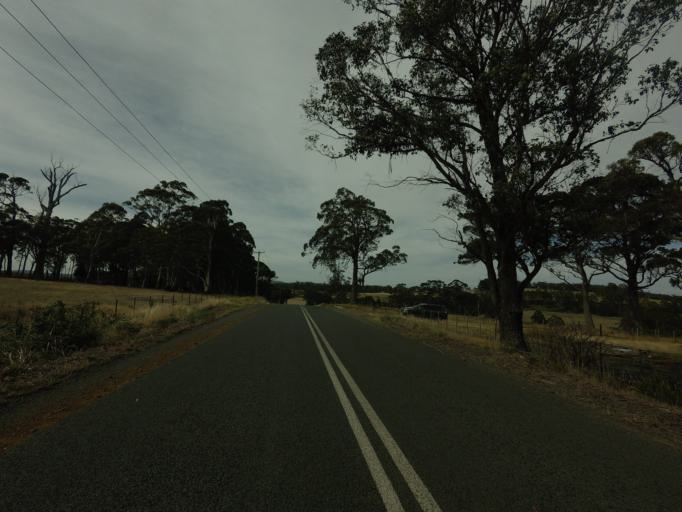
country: AU
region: Tasmania
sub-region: Sorell
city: Sorell
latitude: -42.4087
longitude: 147.4548
